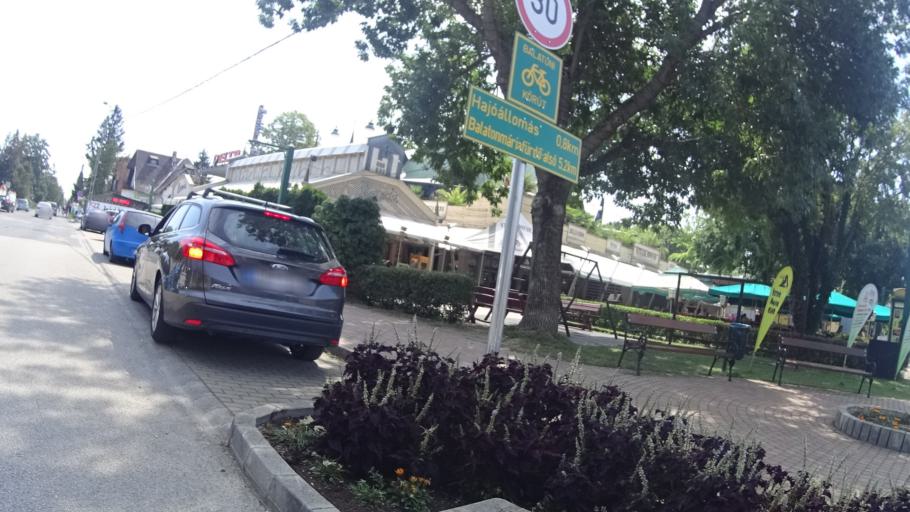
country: HU
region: Somogy
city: Balatonbereny
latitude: 46.7056
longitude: 17.3709
